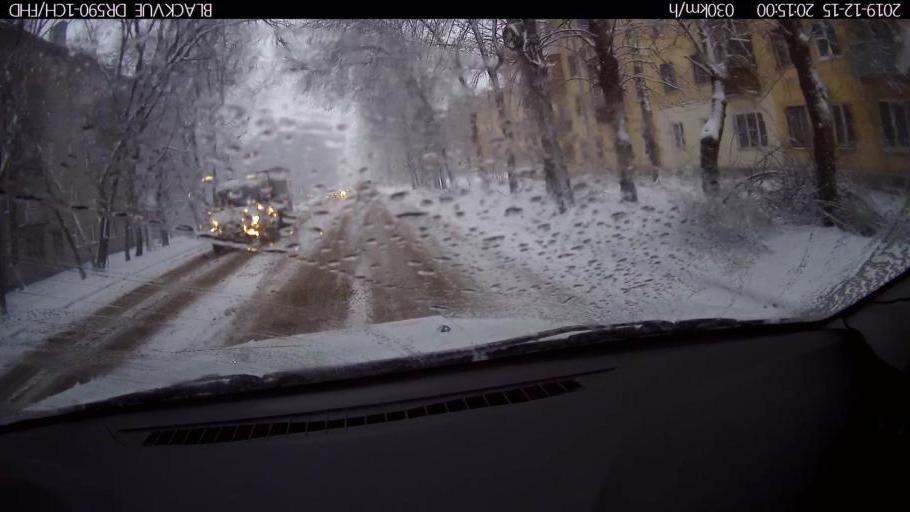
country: RU
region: Nizjnij Novgorod
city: Nizhniy Novgorod
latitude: 56.3113
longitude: 44.0365
